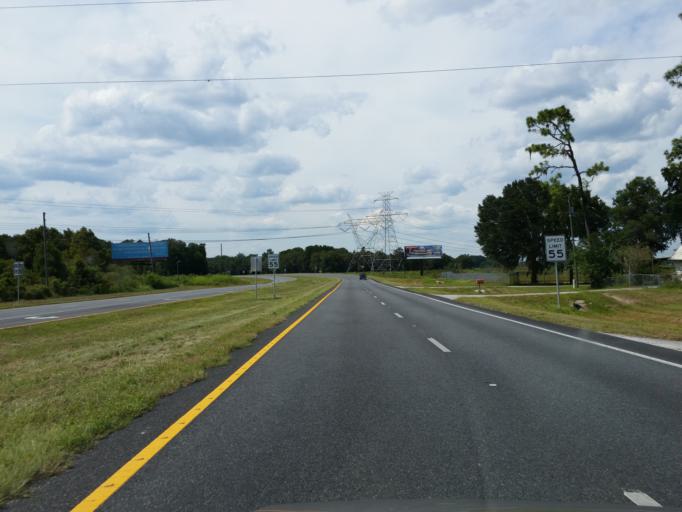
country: US
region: Florida
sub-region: Sumter County
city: Wildwood
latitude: 28.8682
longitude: -82.0810
